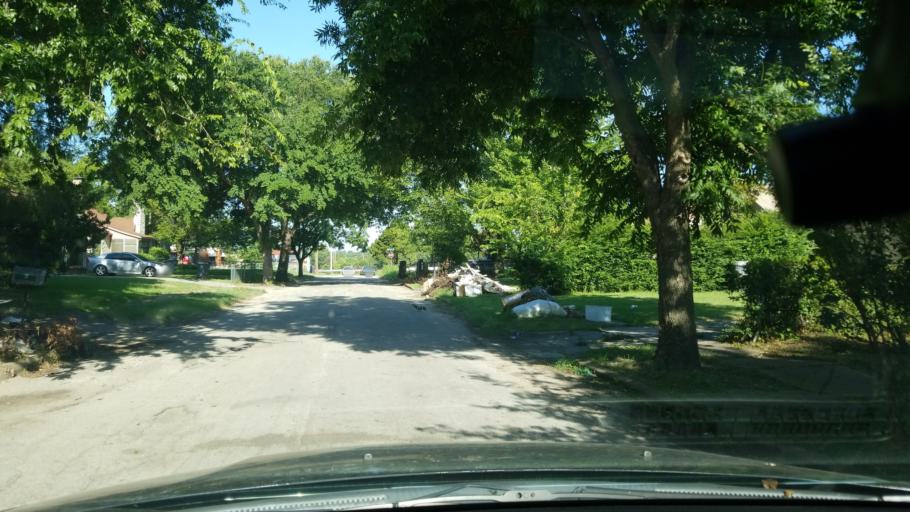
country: US
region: Texas
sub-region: Dallas County
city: Cockrell Hill
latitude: 32.7214
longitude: -96.8255
